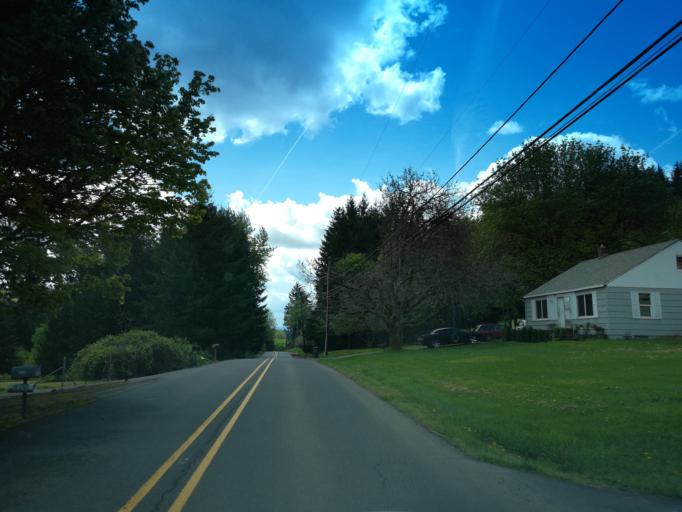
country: US
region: Oregon
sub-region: Clackamas County
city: Damascus
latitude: 45.4287
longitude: -122.4477
